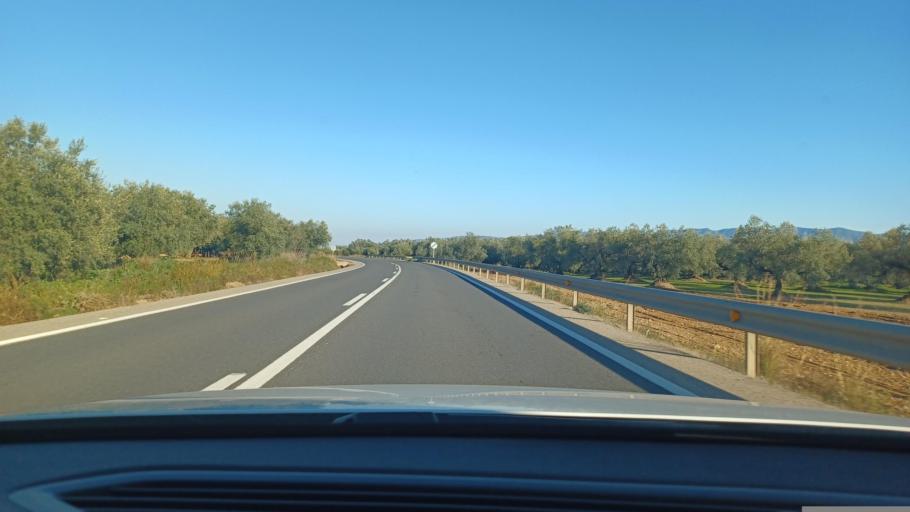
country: ES
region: Catalonia
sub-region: Provincia de Tarragona
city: Ulldecona
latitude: 40.6434
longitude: 0.3778
